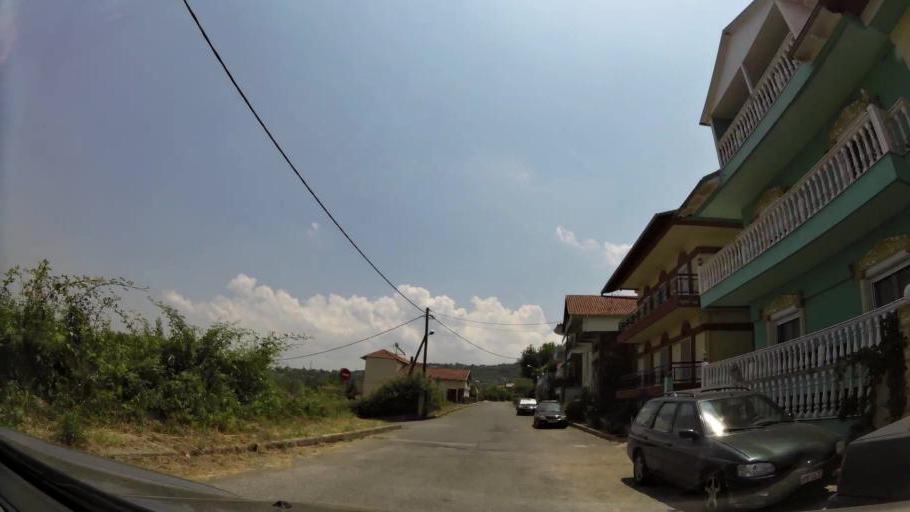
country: GR
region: Central Macedonia
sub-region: Nomos Imathias
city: Veroia
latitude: 40.5148
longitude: 22.1879
